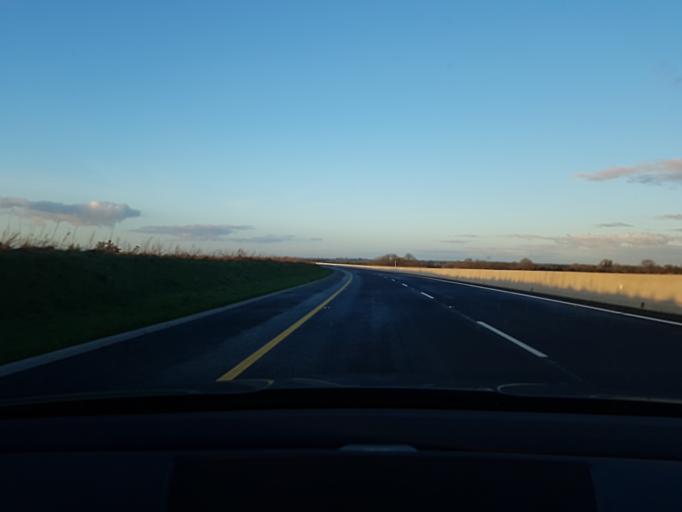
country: IE
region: Connaught
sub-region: County Galway
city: Tuam
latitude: 53.4530
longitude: -8.8477
